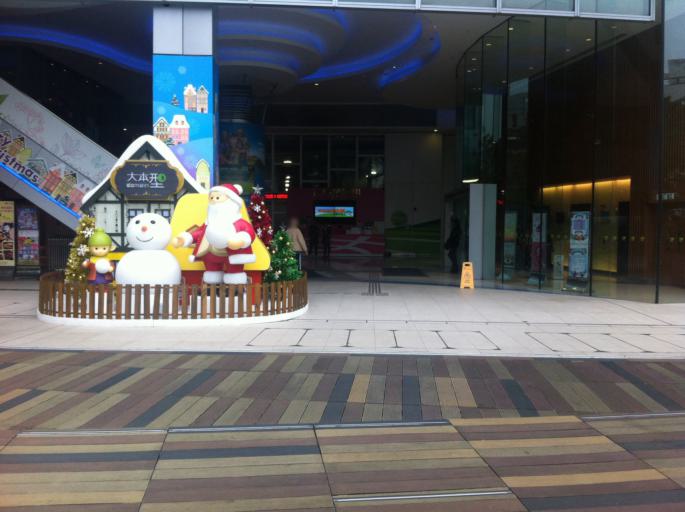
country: HK
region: Kowloon City
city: Kowloon
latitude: 22.2965
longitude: 114.2383
